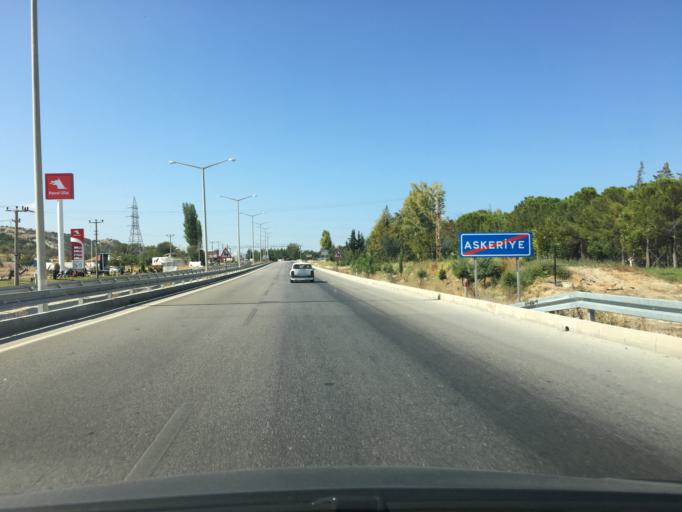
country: TR
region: Burdur
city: Burdur
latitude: 37.7567
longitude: 30.3394
